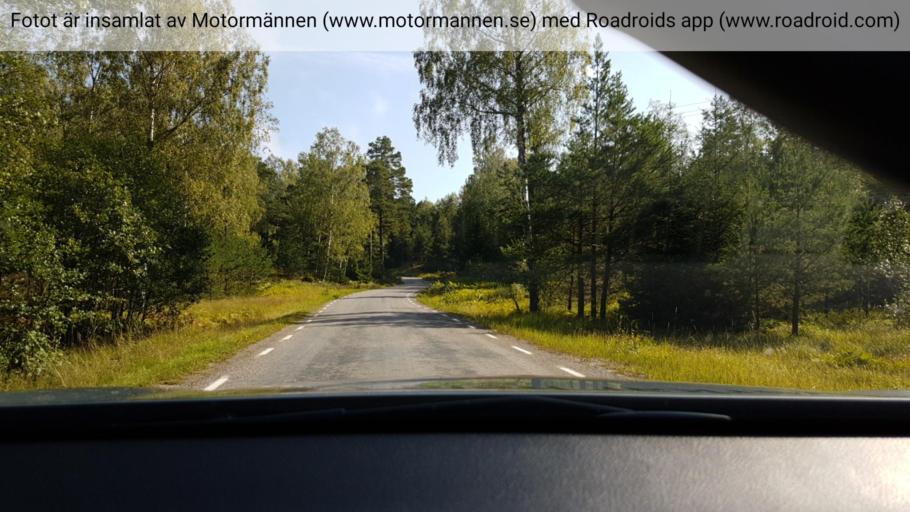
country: SE
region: Stockholm
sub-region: Nynashamns Kommun
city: Osmo
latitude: 58.8772
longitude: 17.7900
